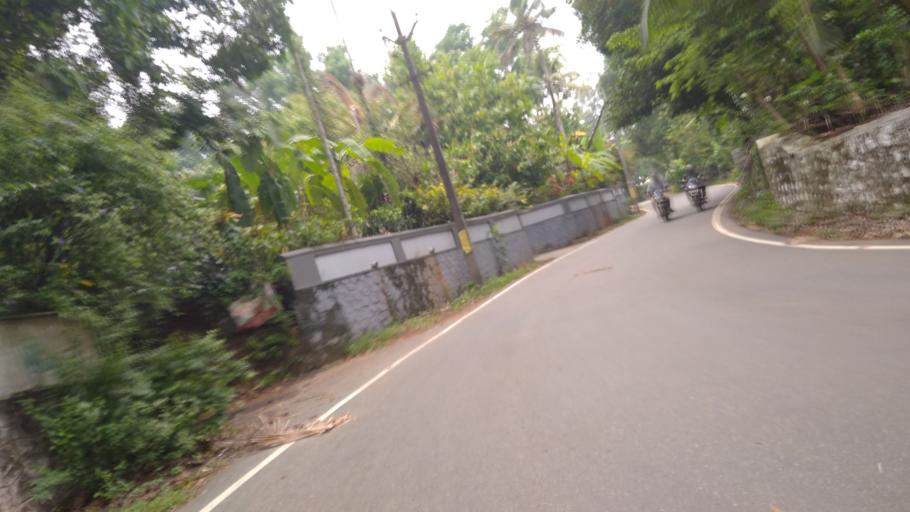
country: IN
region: Kerala
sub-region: Ernakulam
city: Perumpavur
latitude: 10.1188
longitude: 76.5320
